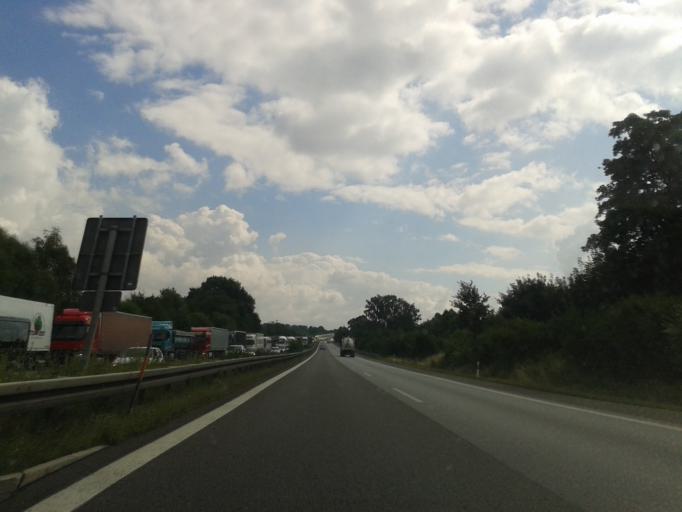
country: DE
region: Saxony
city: Goda
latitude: 51.2019
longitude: 14.2925
